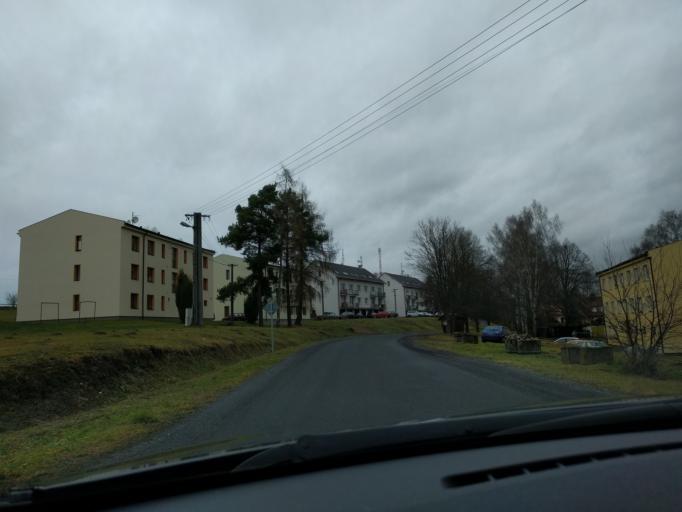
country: CZ
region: Plzensky
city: Bezdruzice
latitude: 49.9372
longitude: 12.9973
